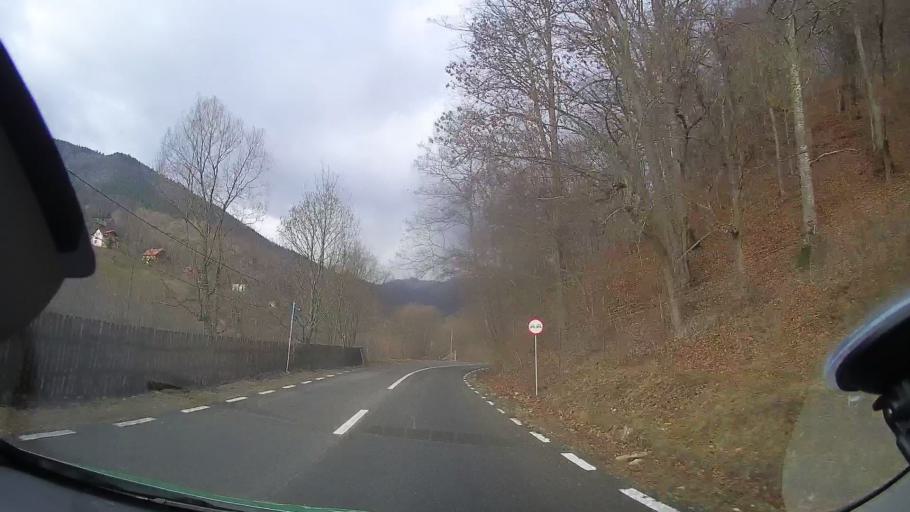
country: RO
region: Cluj
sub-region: Comuna Valea Ierii
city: Valea Ierii
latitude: 46.6398
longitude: 23.3600
